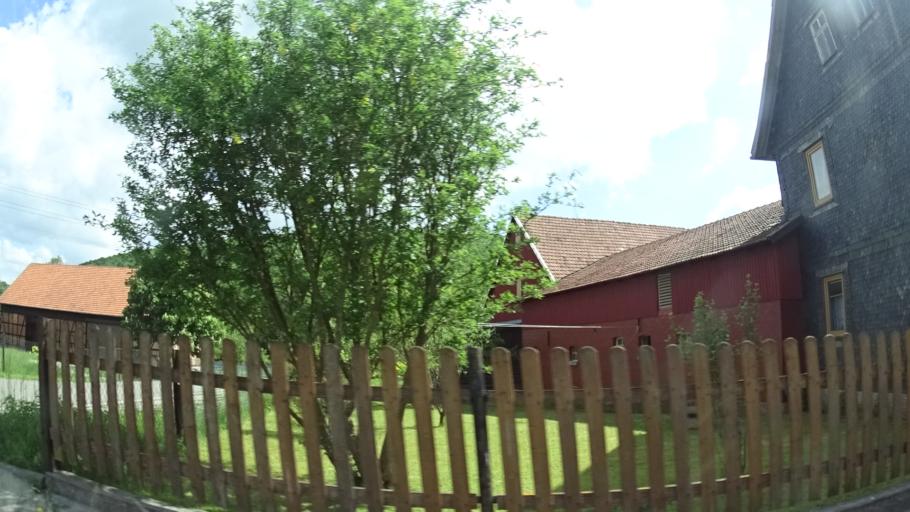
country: DE
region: Thuringia
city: Ritschenhausen
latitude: 50.5111
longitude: 10.4316
